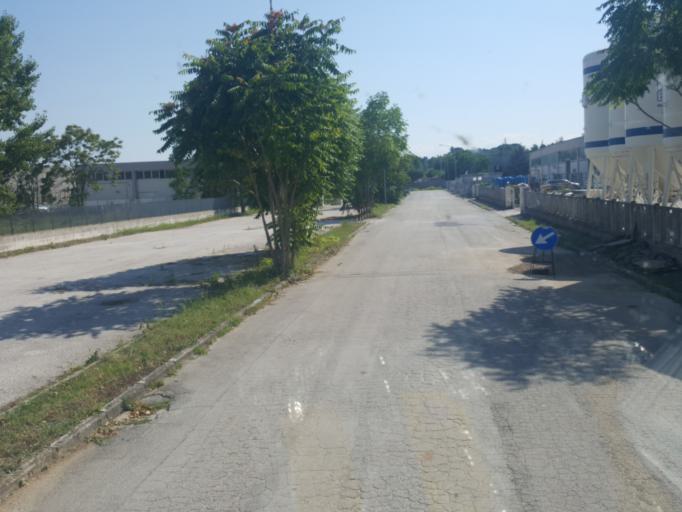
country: IT
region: The Marches
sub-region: Provincia di Ancona
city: Borghetto
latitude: 43.5638
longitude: 13.2904
